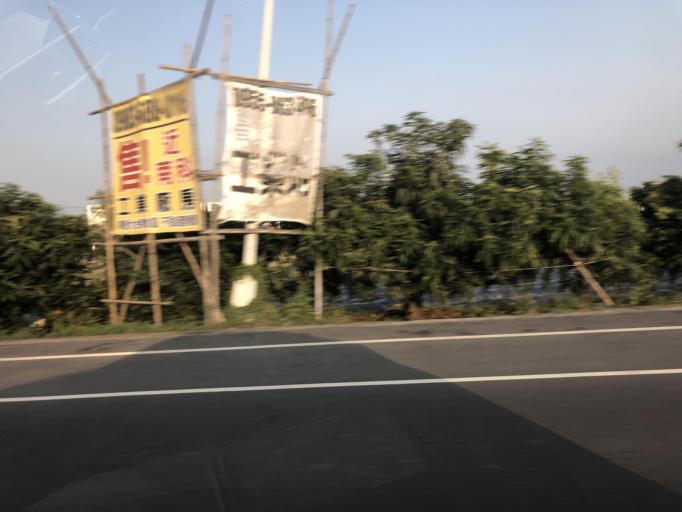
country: TW
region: Taiwan
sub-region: Tainan
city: Tainan
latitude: 23.1215
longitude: 120.2471
